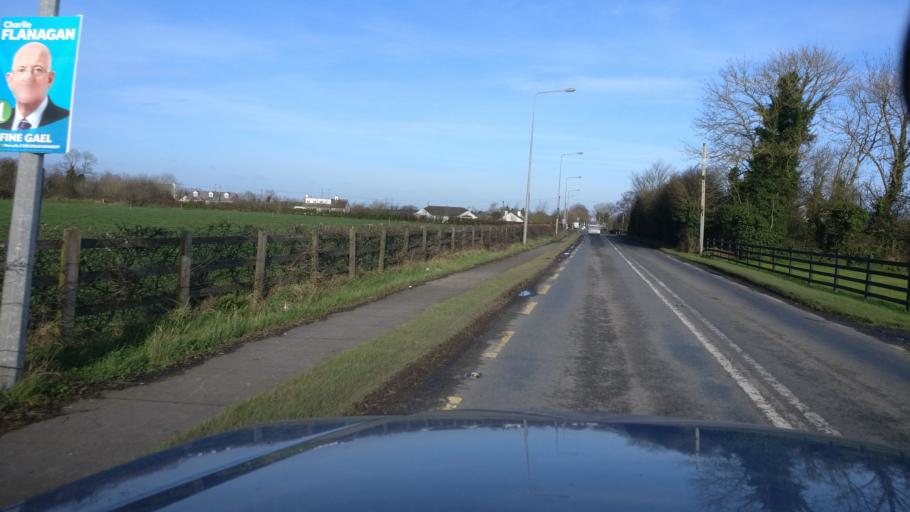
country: IE
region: Leinster
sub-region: Laois
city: Portlaoise
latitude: 53.0269
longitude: -7.2655
